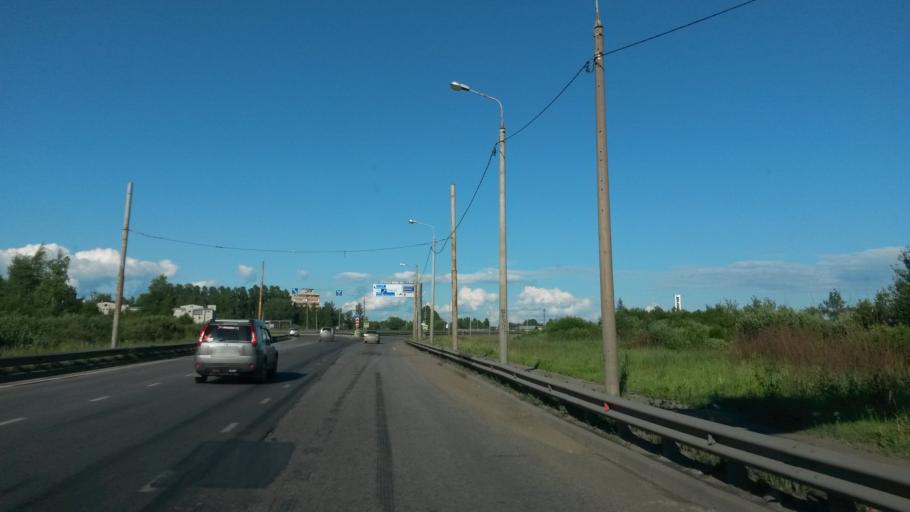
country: RU
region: Jaroslavl
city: Yaroslavl
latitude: 57.6695
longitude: 39.7720
